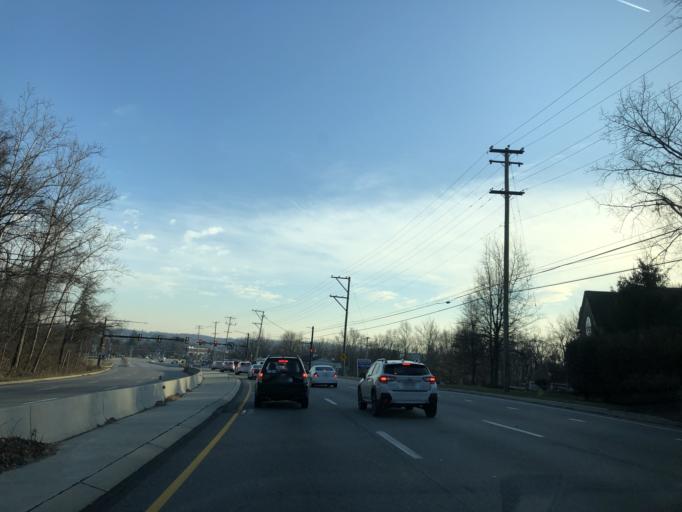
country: US
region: Pennsylvania
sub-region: Chester County
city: Exton
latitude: 40.0415
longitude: -75.6341
